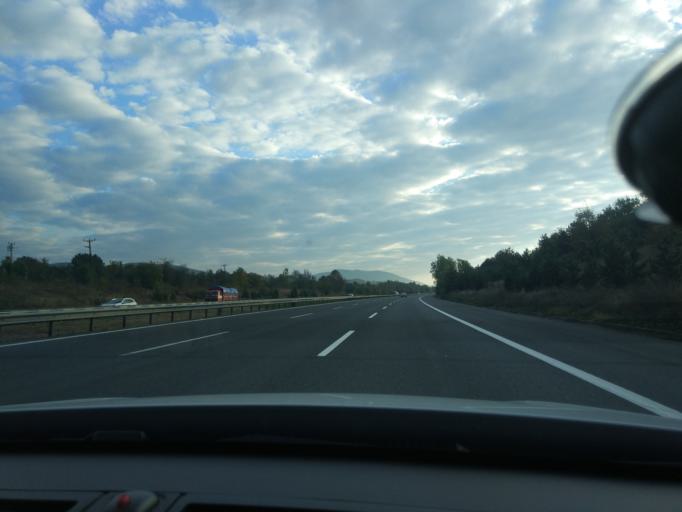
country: TR
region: Sakarya
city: Karadere
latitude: 40.7840
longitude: 30.8087
